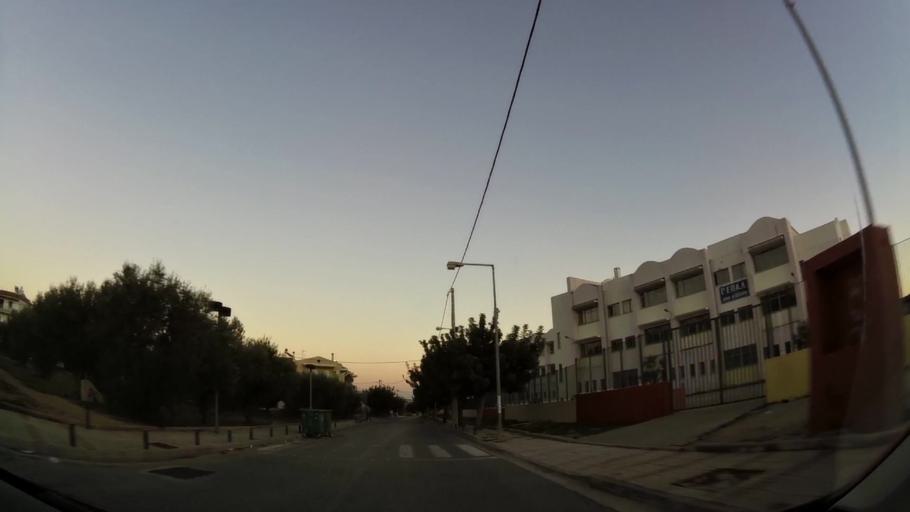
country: GR
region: Attica
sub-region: Nomarchia Dytikis Attikis
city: Ano Liosia
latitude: 38.0822
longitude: 23.6908
